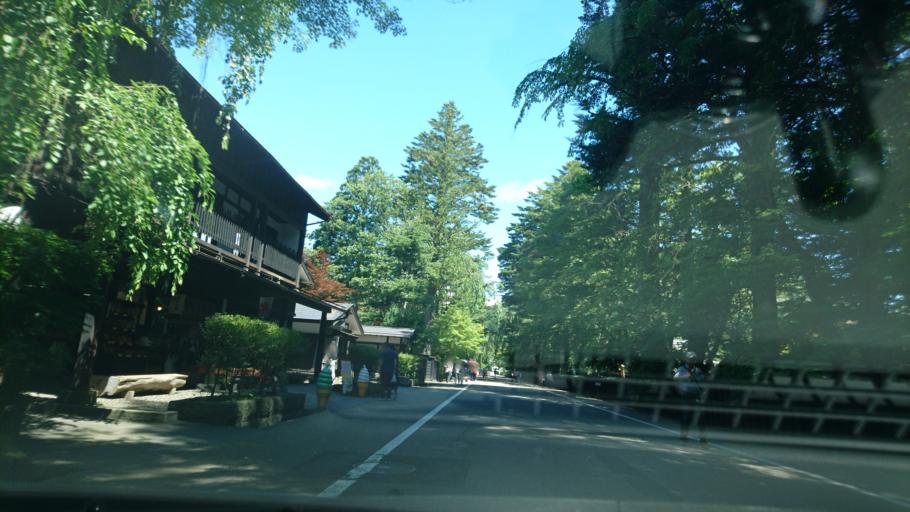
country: JP
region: Akita
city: Kakunodatemachi
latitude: 39.5999
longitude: 140.5615
